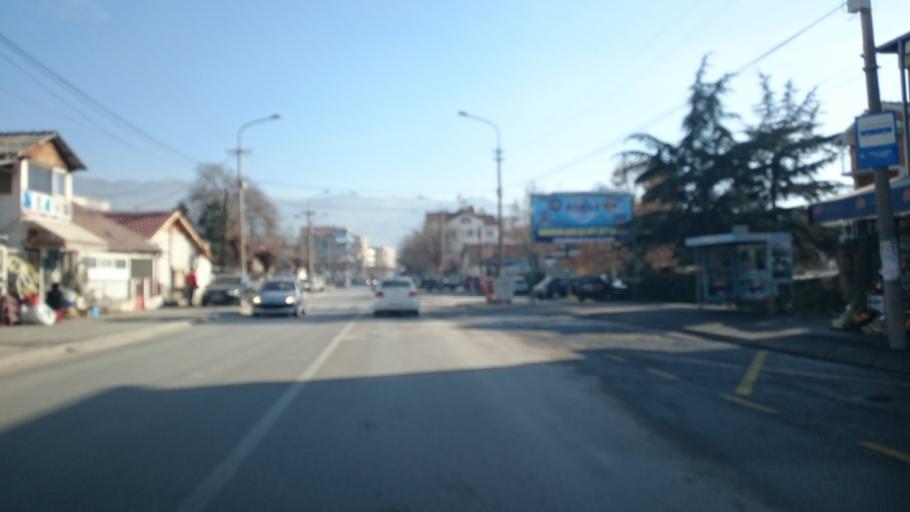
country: MK
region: Prilep
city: Prilep
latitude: 41.3491
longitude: 21.5504
